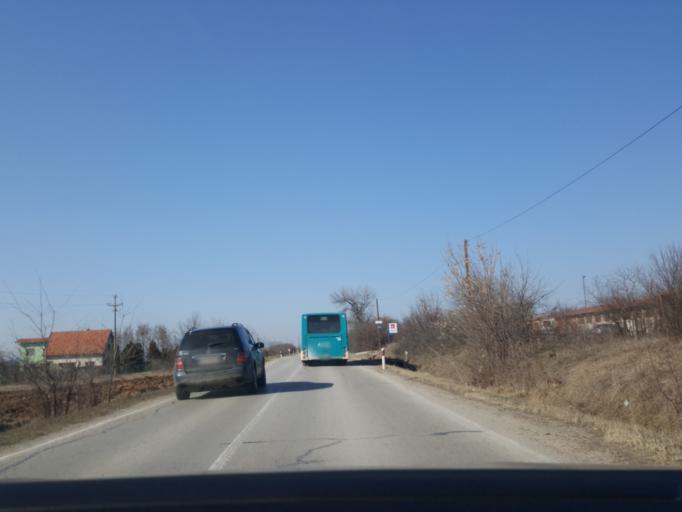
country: RS
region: Central Serbia
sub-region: Nisavski Okrug
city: Nis
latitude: 43.3835
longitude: 21.8201
